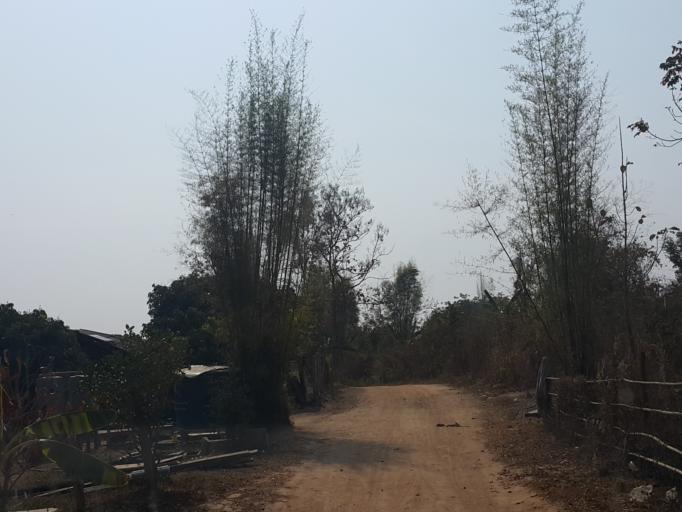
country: TH
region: Chiang Mai
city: Hang Dong
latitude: 18.7257
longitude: 98.8535
